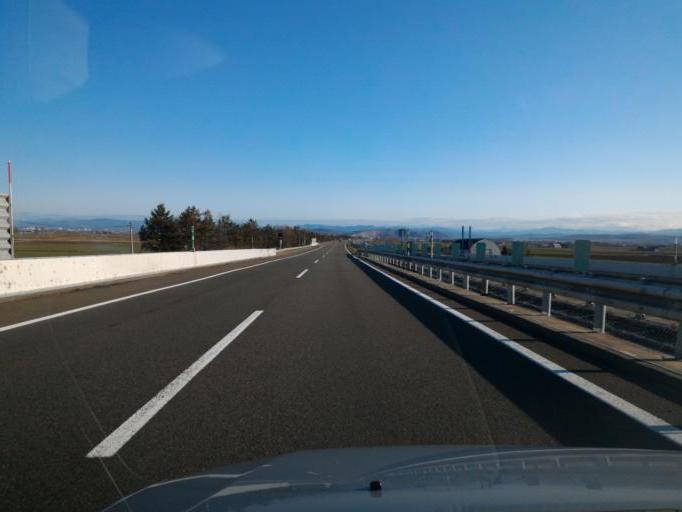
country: JP
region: Hokkaido
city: Iwamizawa
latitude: 43.1496
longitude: 141.6973
